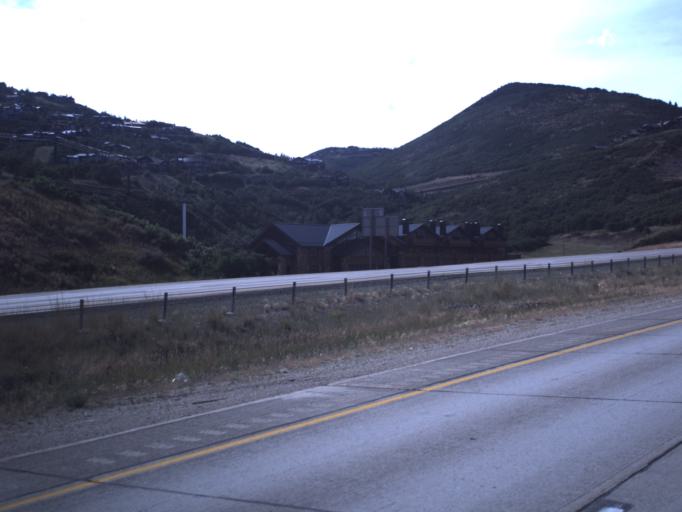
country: US
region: Utah
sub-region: Summit County
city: Park City
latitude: 40.6351
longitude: -111.4494
